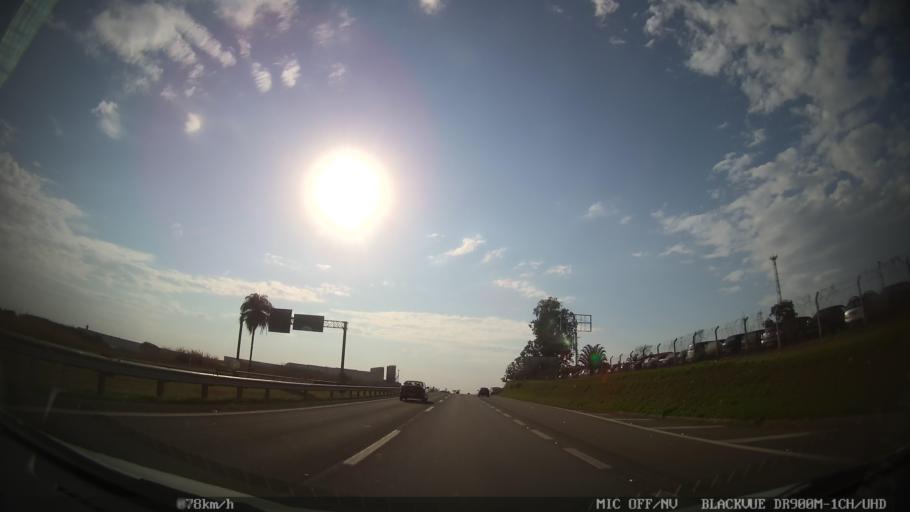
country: BR
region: Sao Paulo
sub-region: Cosmopolis
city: Cosmopolis
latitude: -22.6724
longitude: -47.1616
